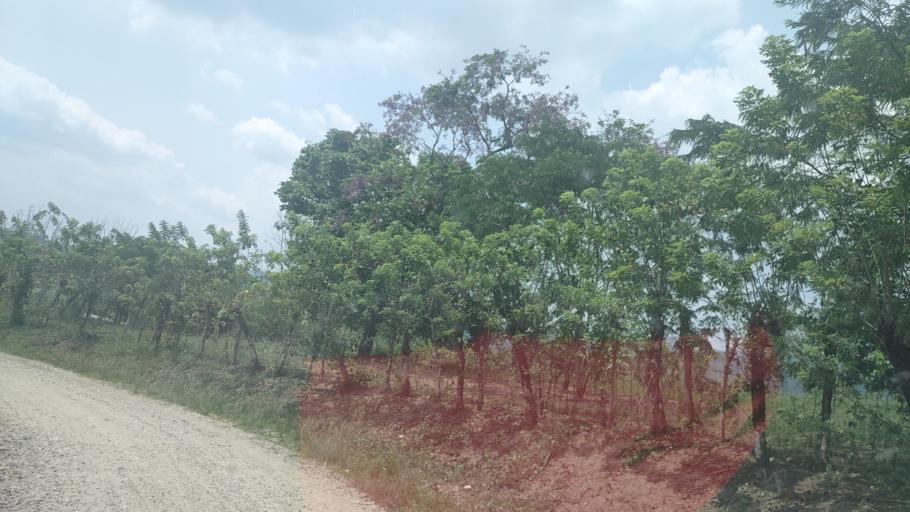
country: MX
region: Chiapas
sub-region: Tecpatan
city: Raudales Malpaso
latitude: 17.2702
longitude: -93.8705
